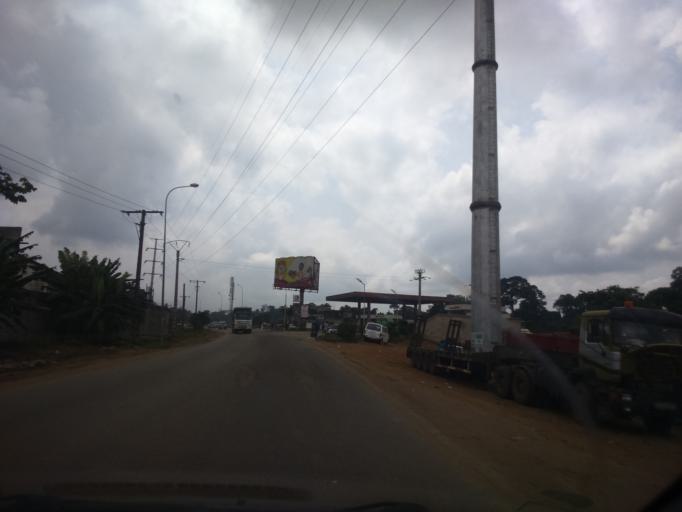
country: CI
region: Lagunes
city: Abobo
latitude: 5.3775
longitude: -4.0762
